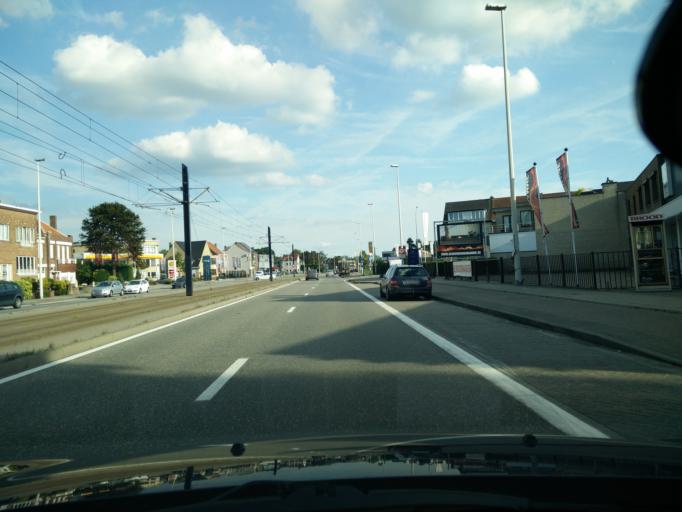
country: BE
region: Flanders
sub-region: Provincie Oost-Vlaanderen
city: Ledeberg
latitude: 51.0289
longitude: 3.7663
